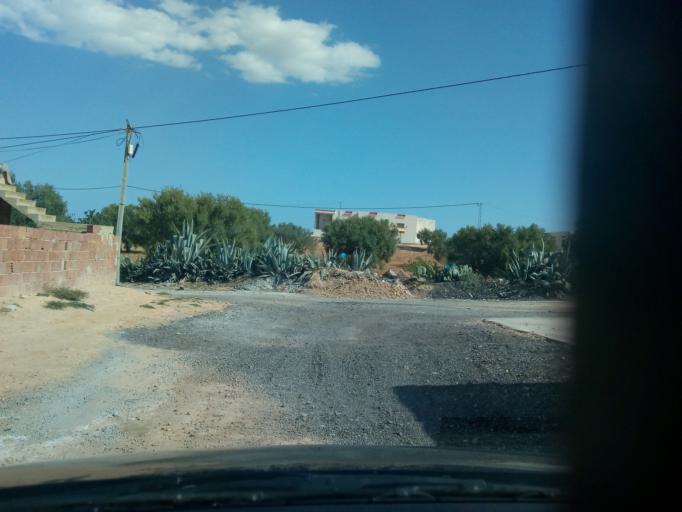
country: TN
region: Safaqis
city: Sfax
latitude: 34.7264
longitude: 10.6083
